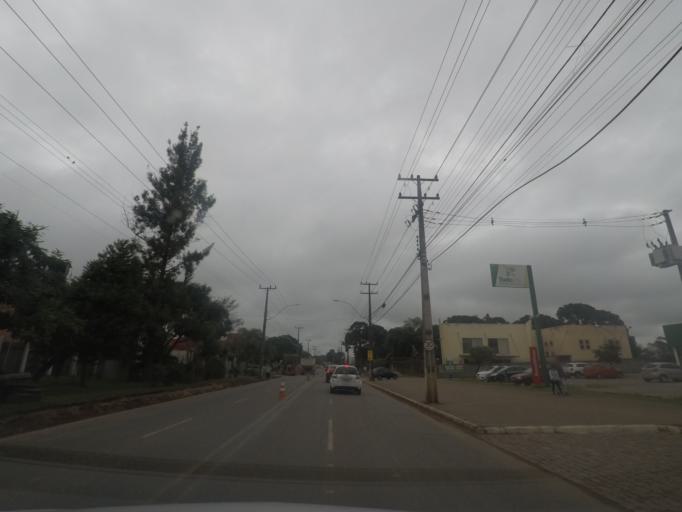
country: BR
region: Parana
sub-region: Piraquara
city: Piraquara
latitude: -25.4512
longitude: -49.0699
